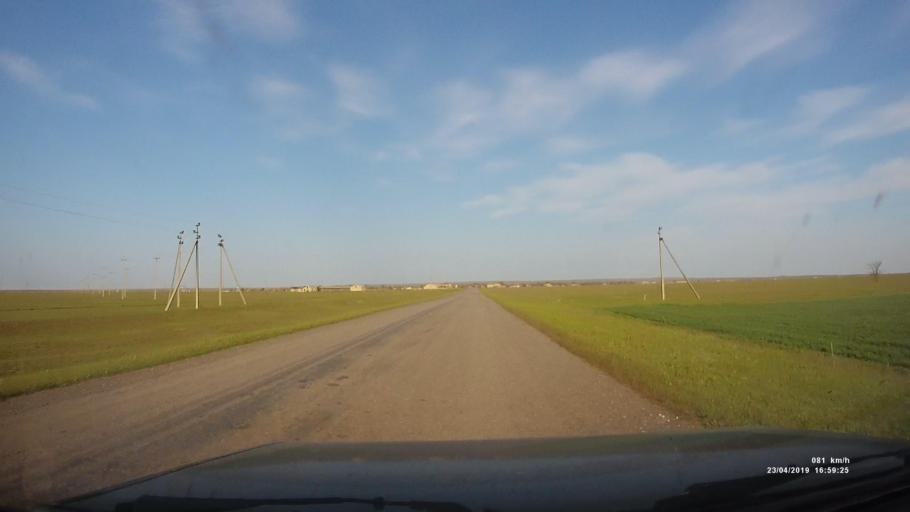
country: RU
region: Kalmykiya
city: Priyutnoye
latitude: 46.3083
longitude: 43.3889
